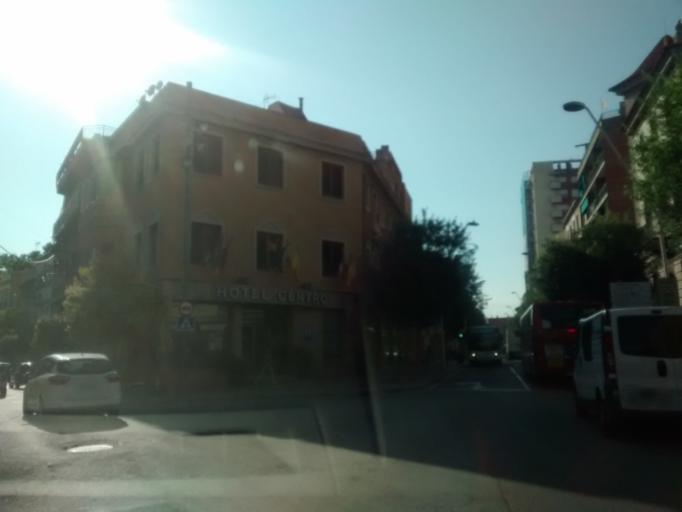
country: ES
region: Catalonia
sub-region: Provincia de Barcelona
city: Sant Feliu de Llobregat
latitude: 41.3804
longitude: 2.0450
